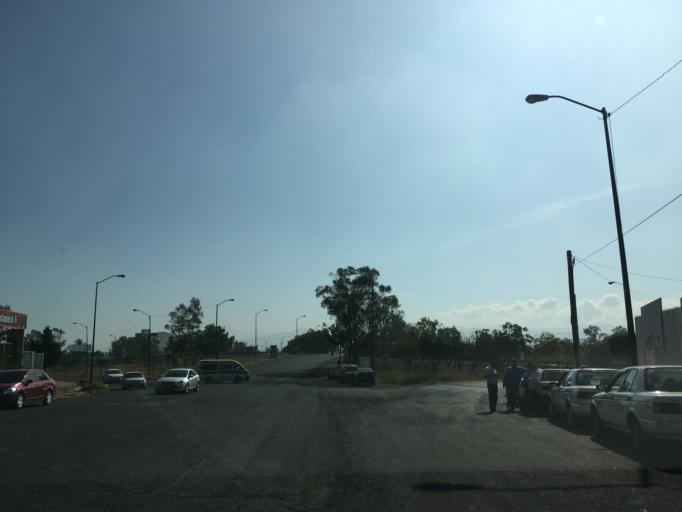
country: MX
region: Michoacan
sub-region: Tarimbaro
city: Fraccionamiento Metropolis II
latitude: 19.7164
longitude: -101.2328
